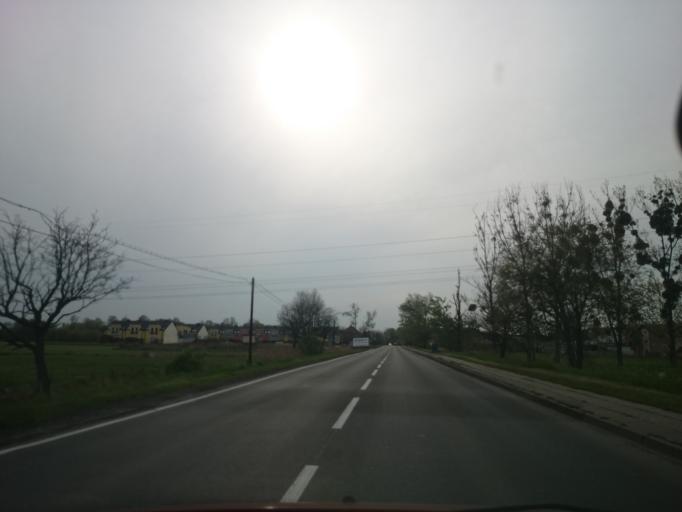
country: PL
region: Opole Voivodeship
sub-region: Powiat opolski
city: Chmielowice
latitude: 50.6818
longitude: 17.8591
